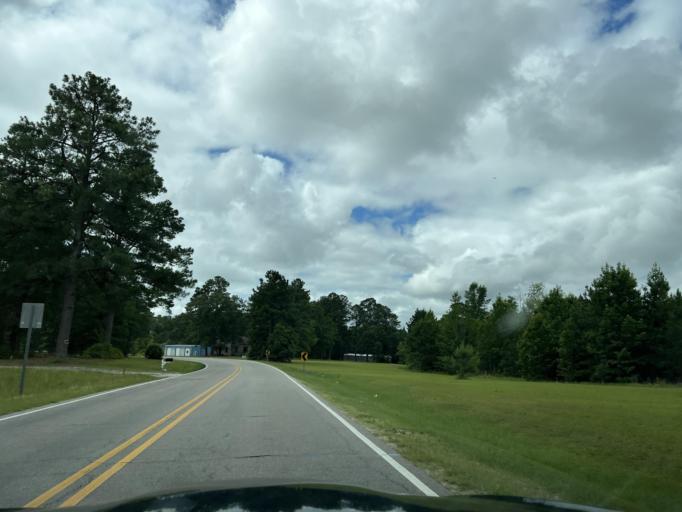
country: US
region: North Carolina
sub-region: Lee County
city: Sanford
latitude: 35.4416
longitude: -79.1733
